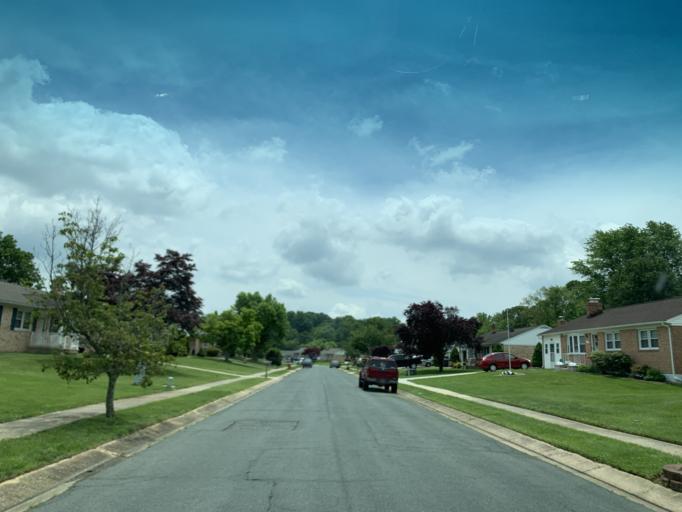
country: US
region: Maryland
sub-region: Harford County
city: Bel Air South
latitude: 39.5381
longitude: -76.2977
